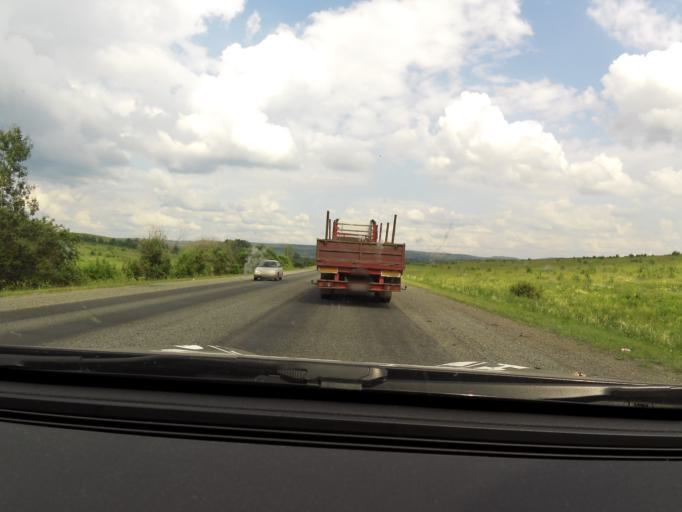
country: RU
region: Sverdlovsk
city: Ufimskiy
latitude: 56.7886
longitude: 58.3308
